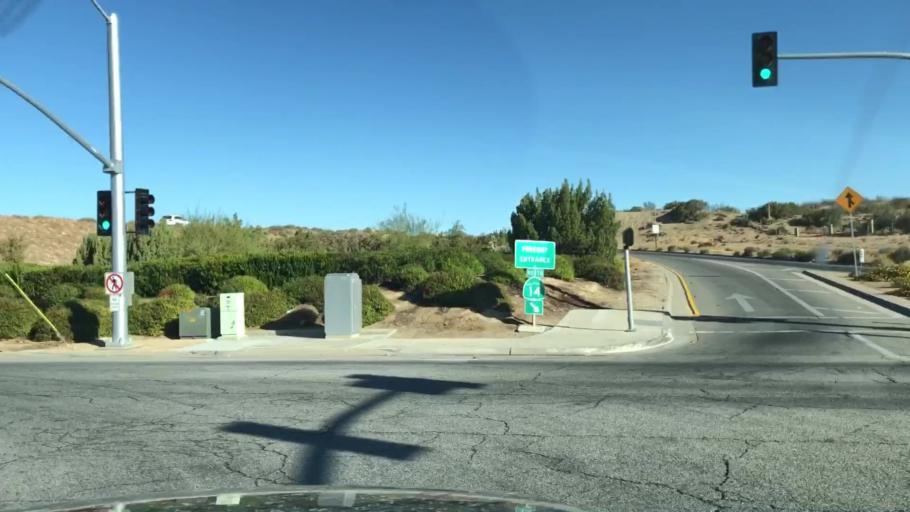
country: US
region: California
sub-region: Los Angeles County
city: Palmdale
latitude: 34.5579
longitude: -118.1318
